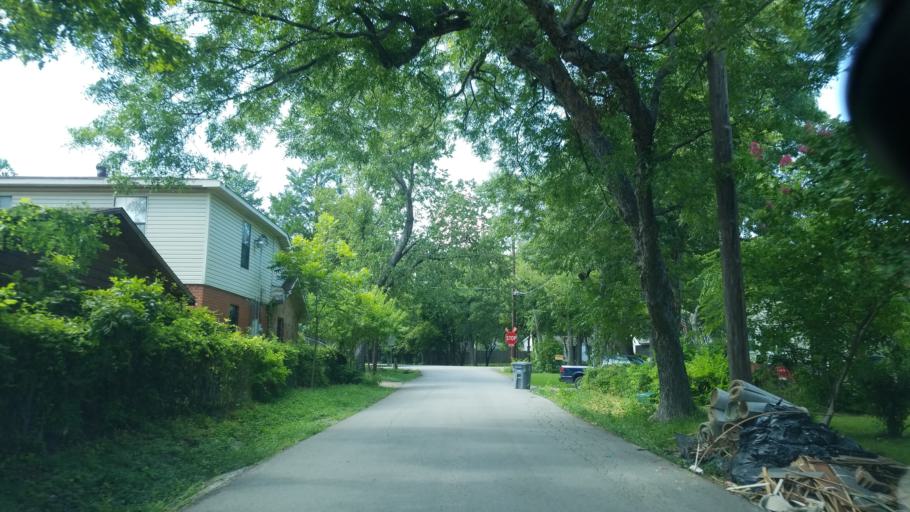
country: US
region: Texas
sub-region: Dallas County
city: Balch Springs
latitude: 32.7669
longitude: -96.6970
